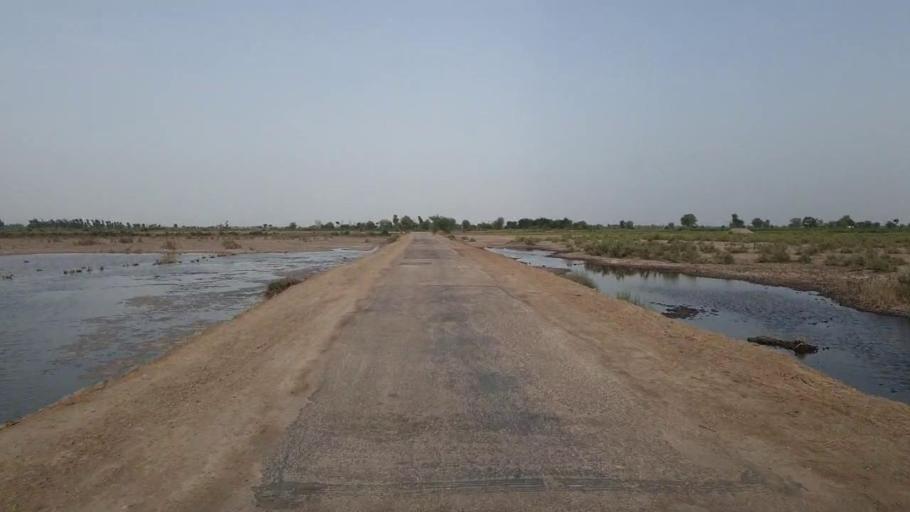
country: PK
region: Sindh
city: Daulatpur
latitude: 26.5463
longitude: 68.0862
